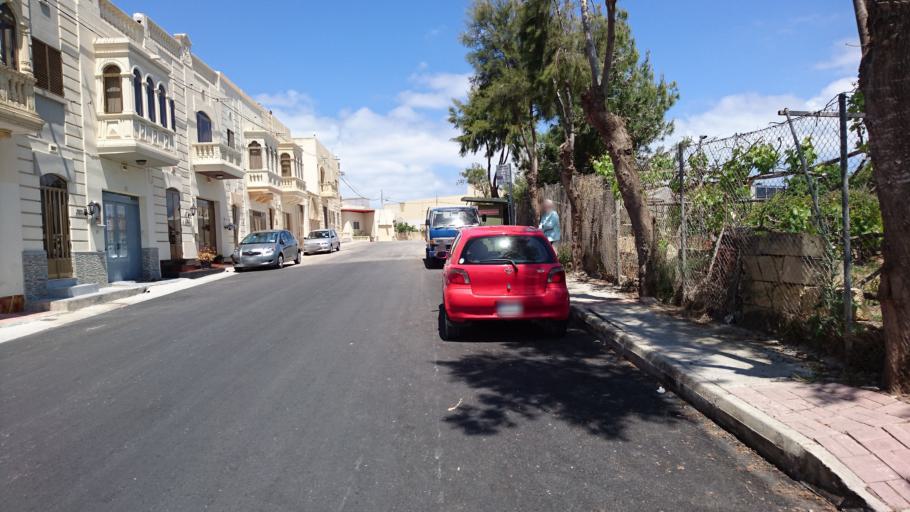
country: MT
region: Ix-Xaghra
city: Xaghra
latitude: 36.0486
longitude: 14.2674
